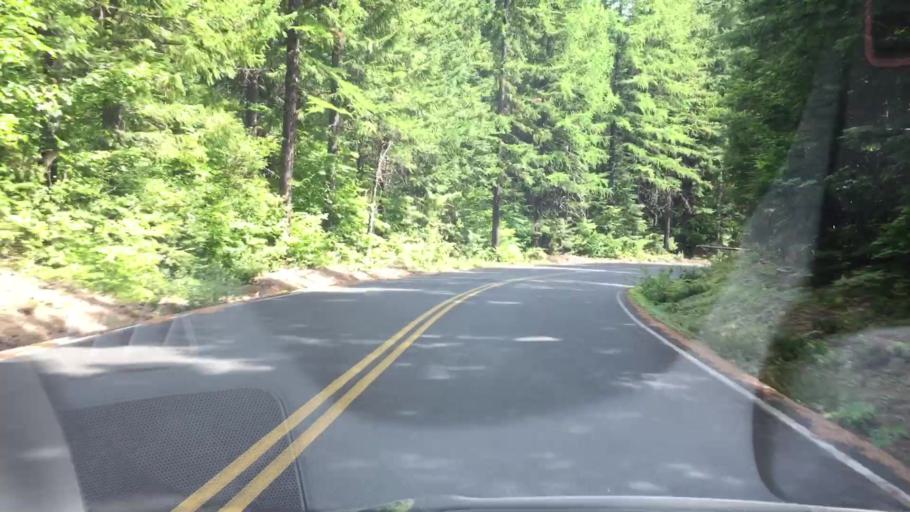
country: US
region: Washington
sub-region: Klickitat County
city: White Salmon
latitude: 46.0881
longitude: -121.6026
